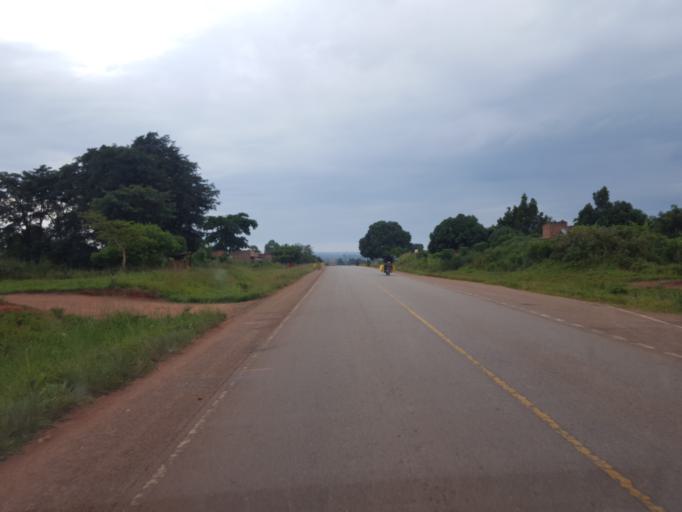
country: UG
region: Central Region
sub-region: Kyankwanzi District
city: Kyankwanzi
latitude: 1.1132
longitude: 31.6087
